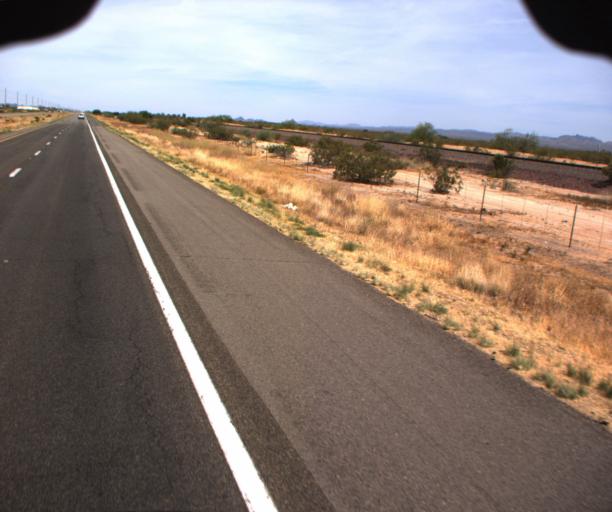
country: US
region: Arizona
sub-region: Maricopa County
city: Sun City West
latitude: 33.7577
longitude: -112.5025
